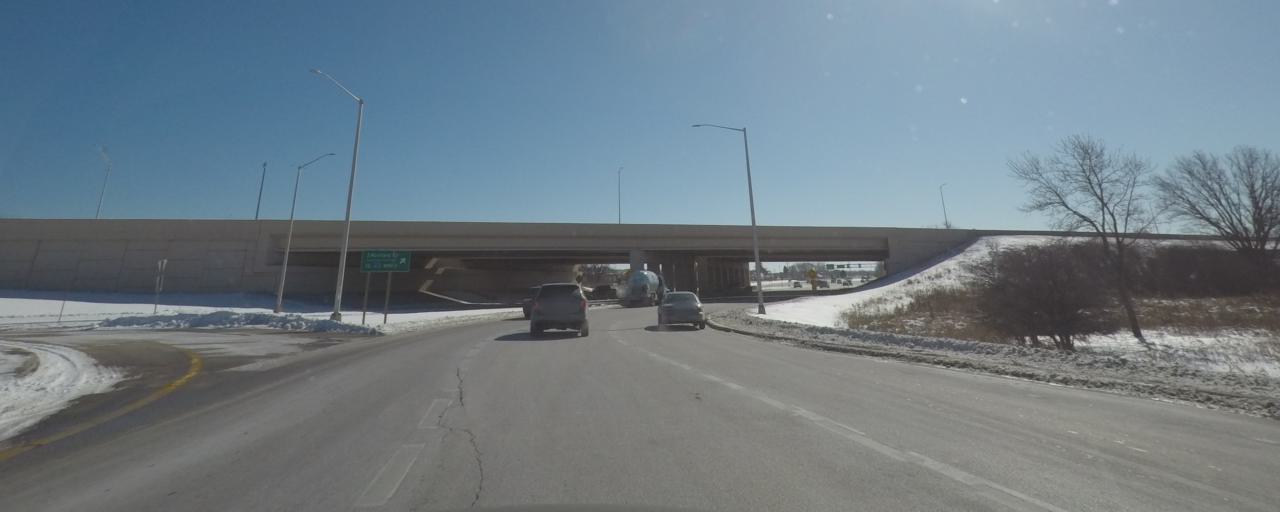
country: US
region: Wisconsin
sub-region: Waukesha County
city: New Berlin
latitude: 42.9534
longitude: -88.1093
